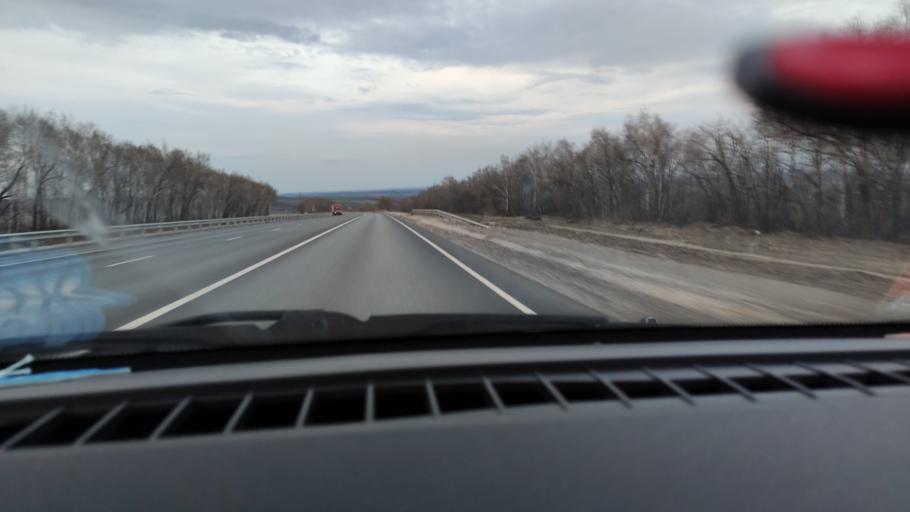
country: RU
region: Saratov
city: Sinodskoye
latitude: 51.9046
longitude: 46.5480
